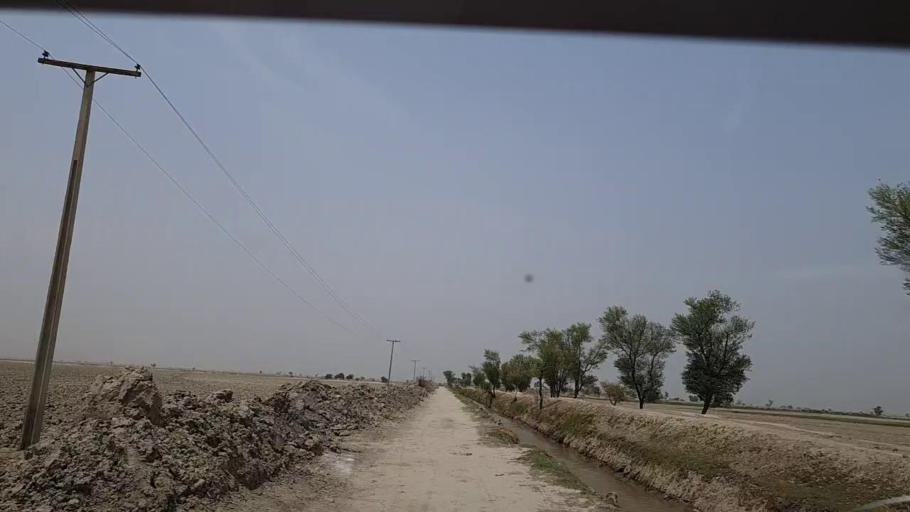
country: PK
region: Sindh
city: Khairpur Nathan Shah
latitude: 27.0485
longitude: 67.6190
